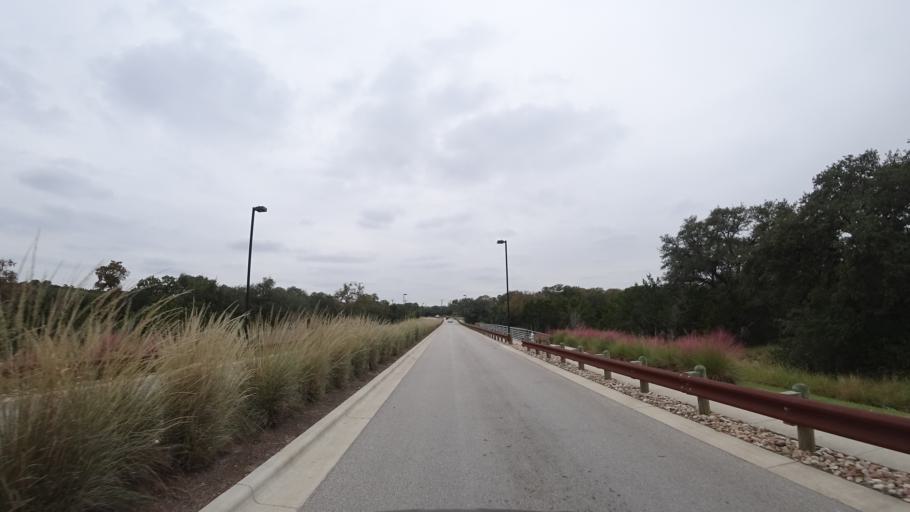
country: US
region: Texas
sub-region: Travis County
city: Shady Hollow
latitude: 30.1777
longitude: -97.9052
